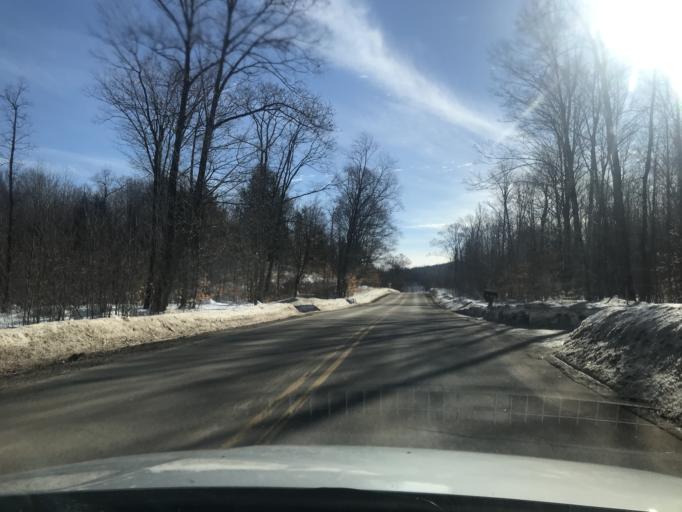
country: US
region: Michigan
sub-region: Dickinson County
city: Kingsford
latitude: 45.4070
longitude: -88.3821
